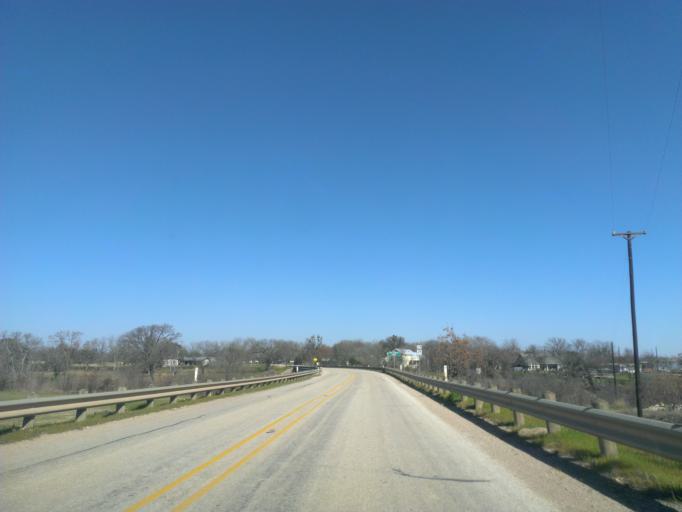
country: US
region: Texas
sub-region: Williamson County
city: Hutto
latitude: 30.6341
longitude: -97.5426
